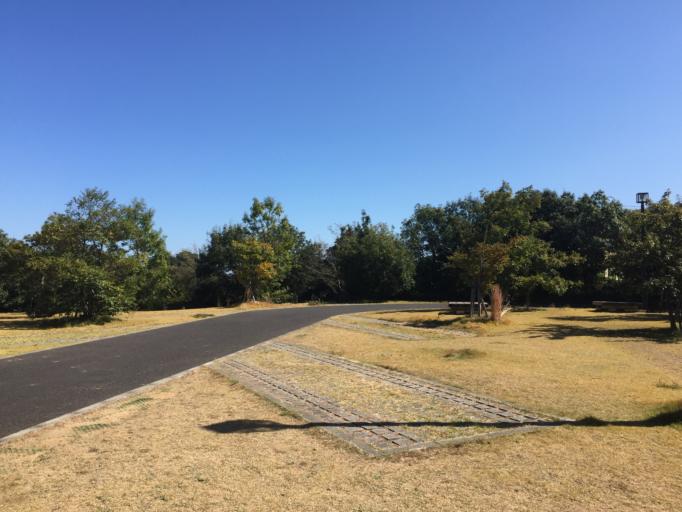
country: JP
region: Kagawa
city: Shido
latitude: 34.2756
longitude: 134.2651
